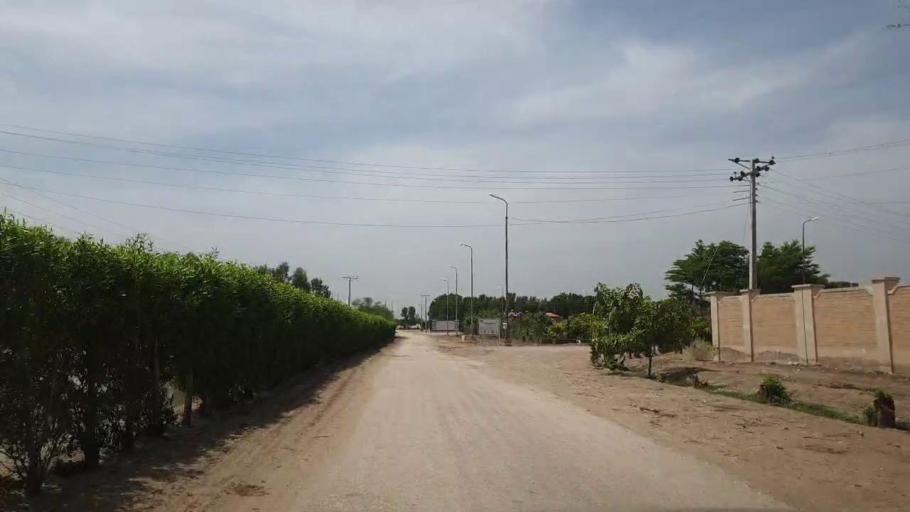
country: PK
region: Sindh
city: Kot Diji
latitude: 27.0917
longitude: 69.0759
